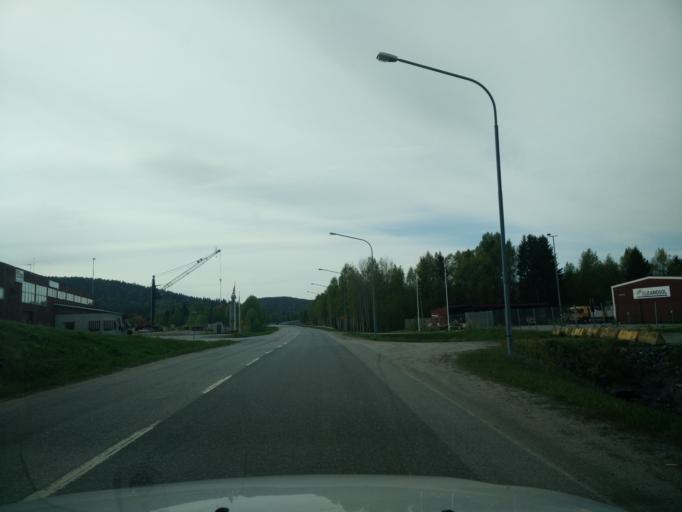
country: SE
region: Vaesternorrland
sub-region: OErnskoeldsviks Kommun
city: Bjasta
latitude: 63.1990
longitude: 18.4979
